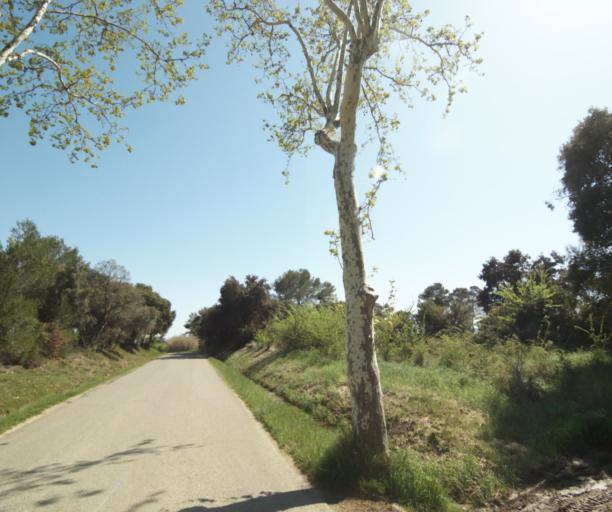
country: FR
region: Languedoc-Roussillon
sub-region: Departement de l'Herault
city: Saint-Drezery
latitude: 43.7219
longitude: 3.9870
